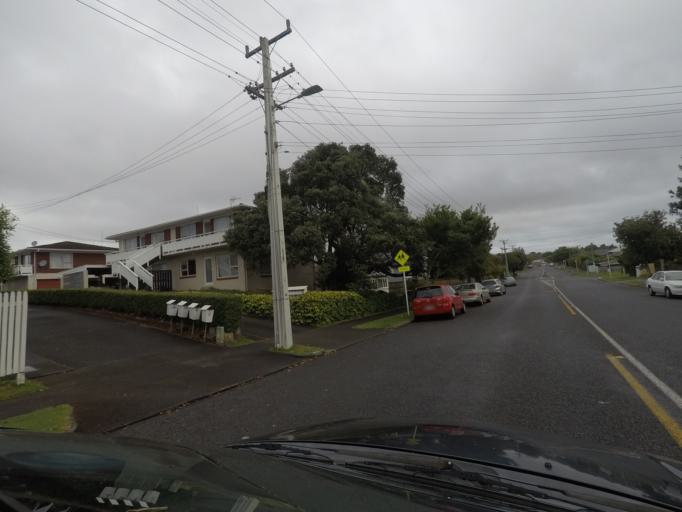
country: NZ
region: Auckland
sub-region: Auckland
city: Auckland
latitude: -36.8862
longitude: 174.7332
